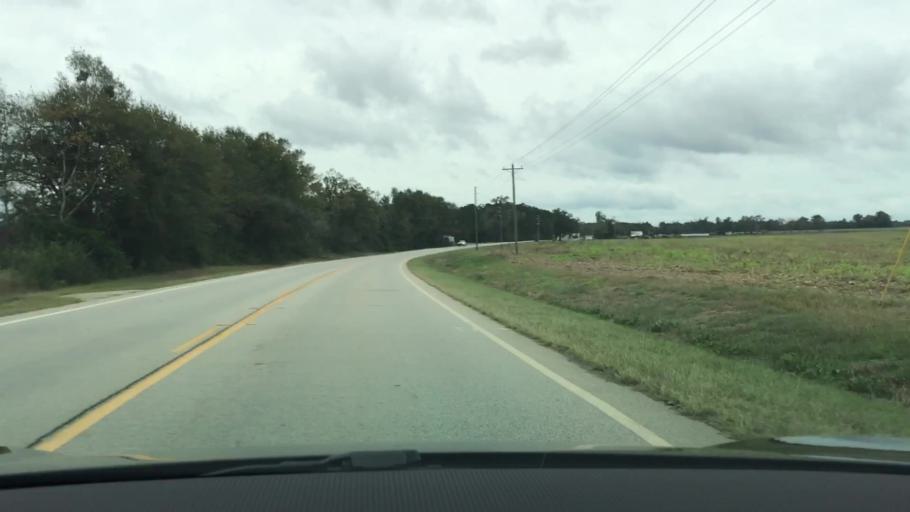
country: US
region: Georgia
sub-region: Jefferson County
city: Wrens
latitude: 33.1810
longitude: -82.4536
